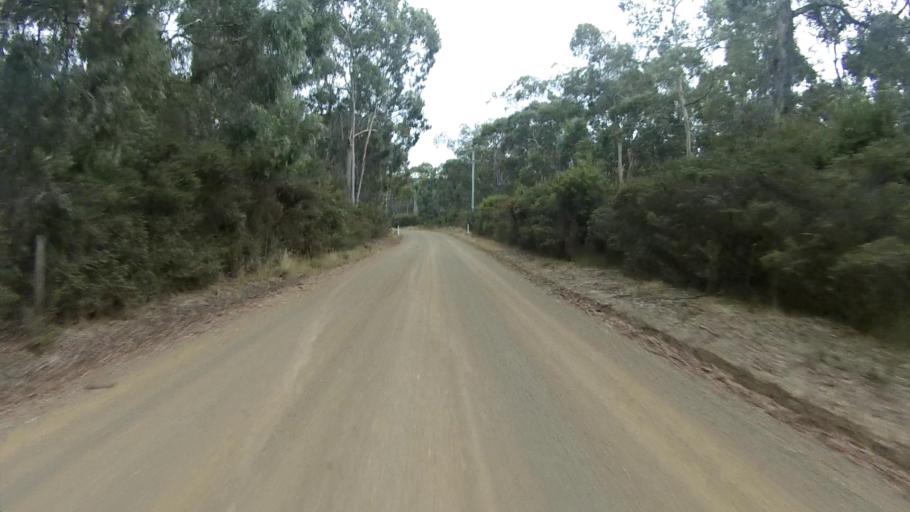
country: AU
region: Tasmania
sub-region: Huon Valley
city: Cygnet
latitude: -43.2437
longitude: 147.1016
